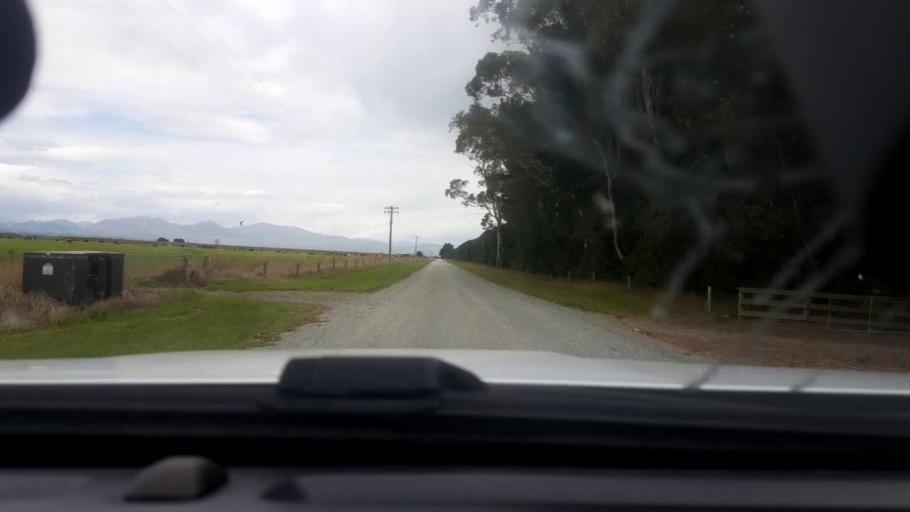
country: NZ
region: Canterbury
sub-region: Timaru District
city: Pleasant Point
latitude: -44.1496
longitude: 171.3931
